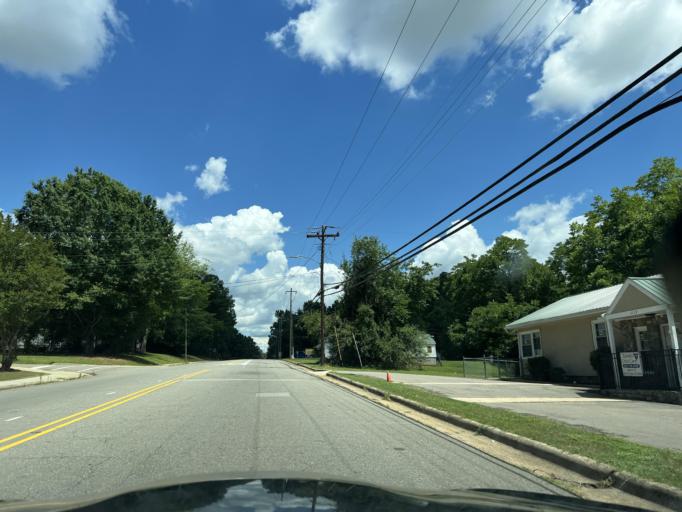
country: US
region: North Carolina
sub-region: Lee County
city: Sanford
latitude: 35.4677
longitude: -79.1679
